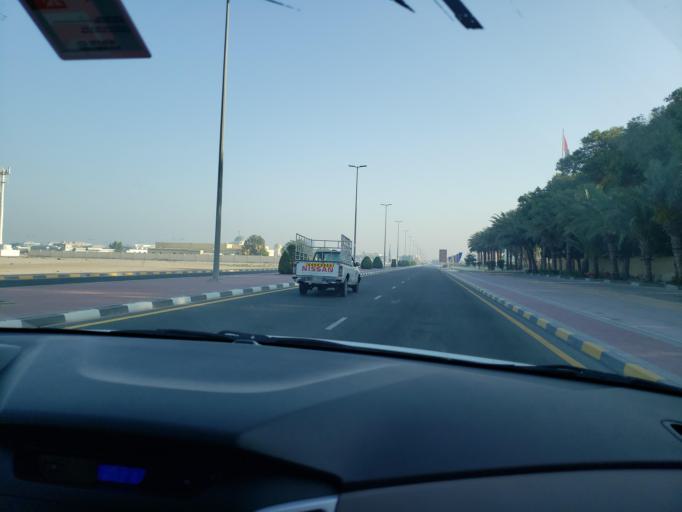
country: AE
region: Umm al Qaywayn
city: Umm al Qaywayn
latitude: 25.5645
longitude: 55.5642
